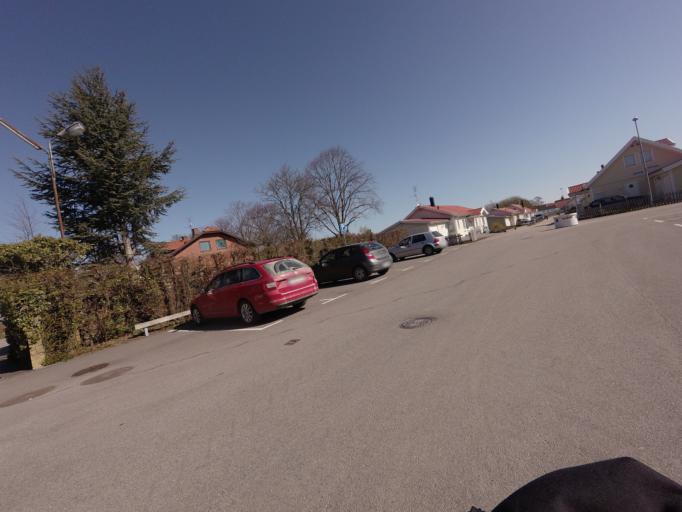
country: SE
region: Skane
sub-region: Malmo
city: Oxie
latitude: 55.4636
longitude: 13.1356
